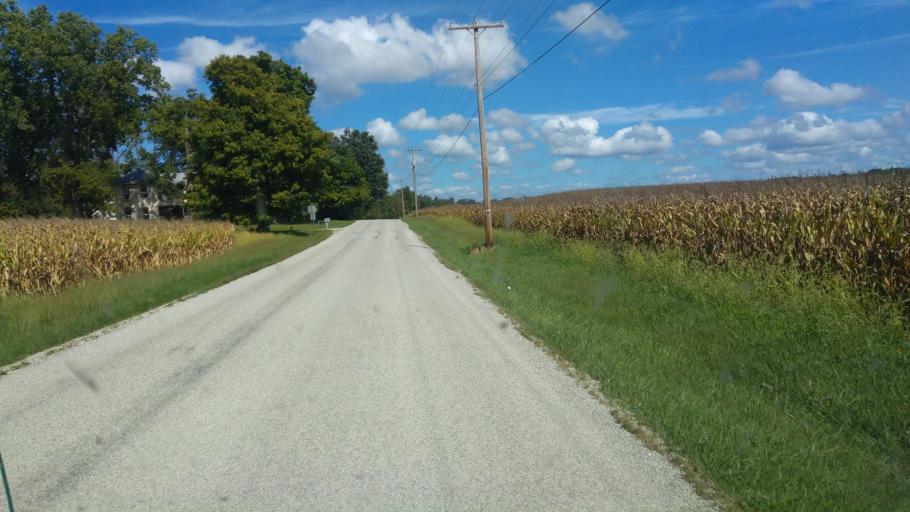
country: US
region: Ohio
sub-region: Richland County
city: Shelby
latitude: 40.9023
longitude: -82.6550
